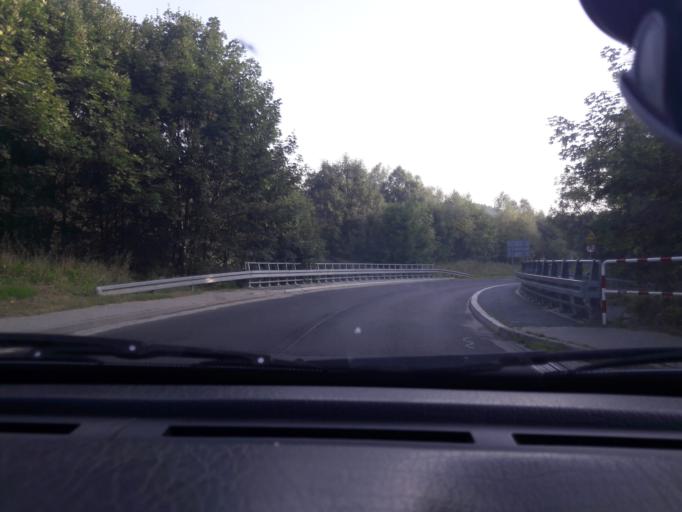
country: PL
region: Lesser Poland Voivodeship
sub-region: Powiat suski
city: Zawoja
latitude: 49.6357
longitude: 19.5282
